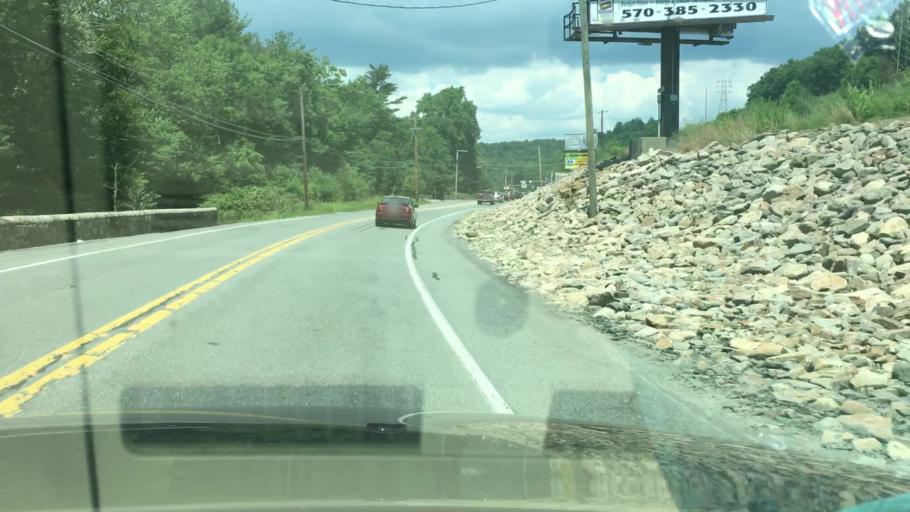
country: US
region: Pennsylvania
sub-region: Schuylkill County
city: Minersville
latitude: 40.6682
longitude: -76.2358
